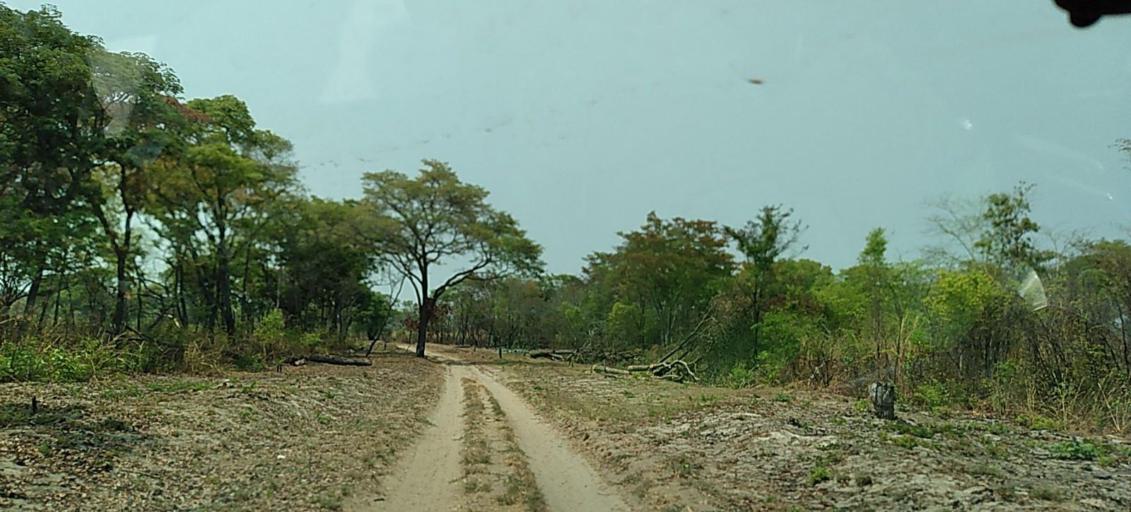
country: ZM
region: Western
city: Lukulu
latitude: -13.9640
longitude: 23.2260
